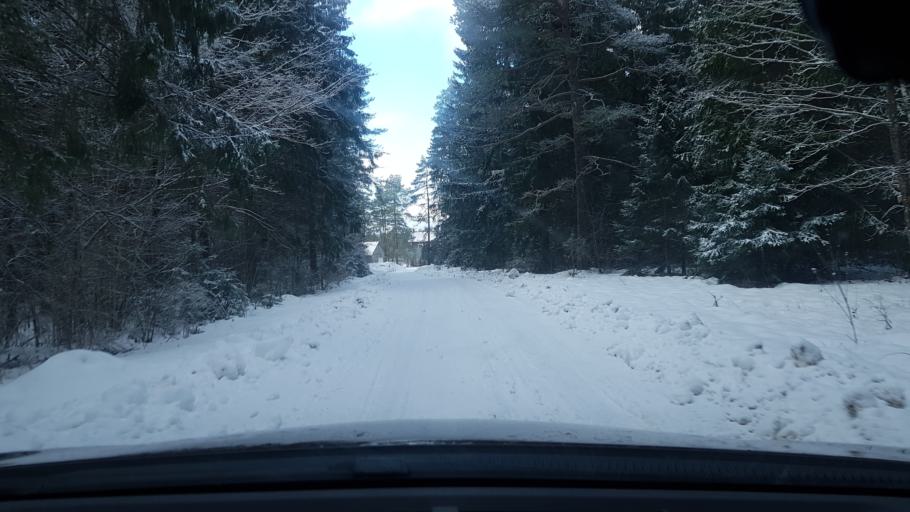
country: EE
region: Harju
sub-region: Keila linn
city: Keila
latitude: 59.2810
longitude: 24.2698
